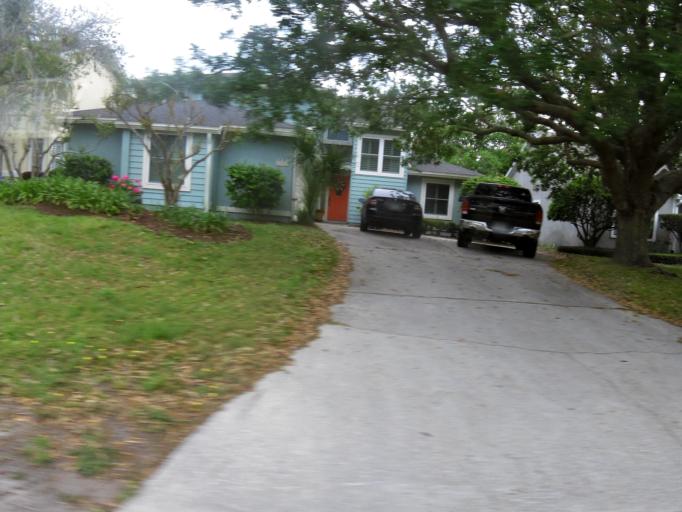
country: US
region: Florida
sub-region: Duval County
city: Atlantic Beach
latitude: 30.3476
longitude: -81.3986
